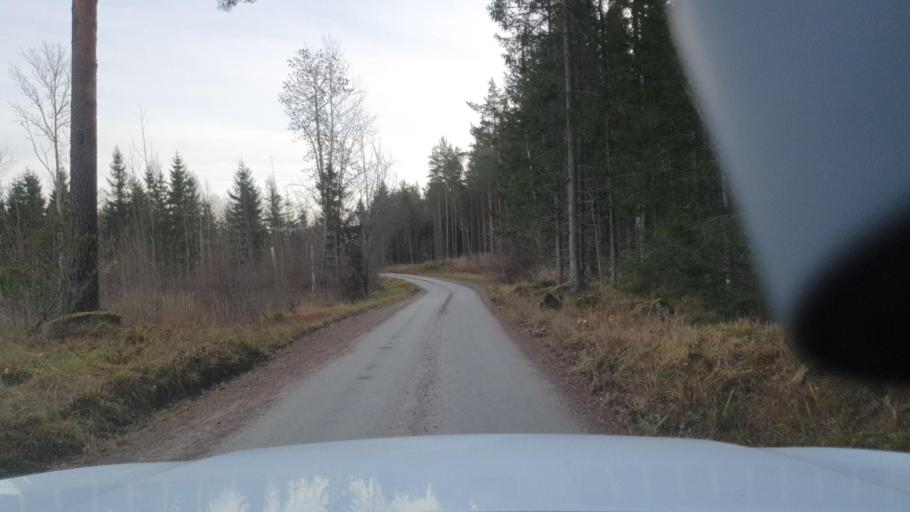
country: SE
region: Uppsala
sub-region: Alvkarleby Kommun
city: AElvkarleby
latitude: 60.4830
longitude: 17.4962
